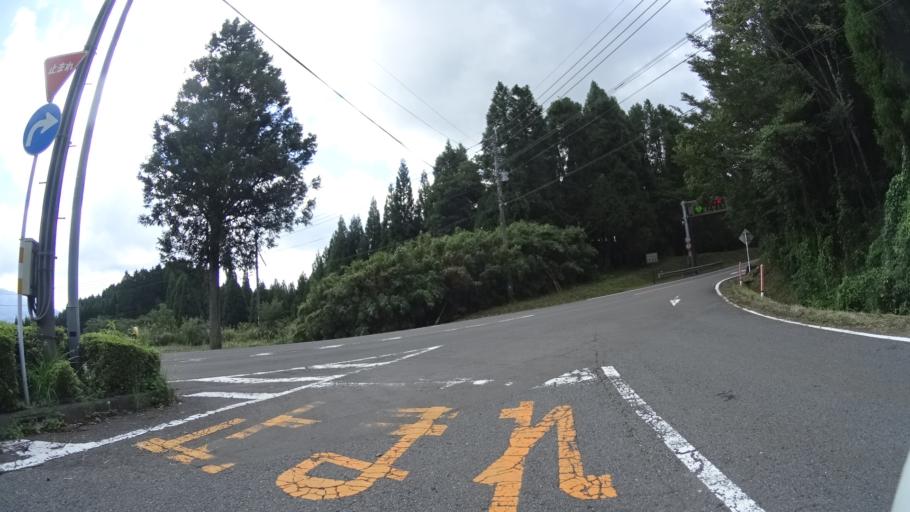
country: JP
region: Oita
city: Tsukawaki
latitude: 33.2494
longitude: 131.2952
